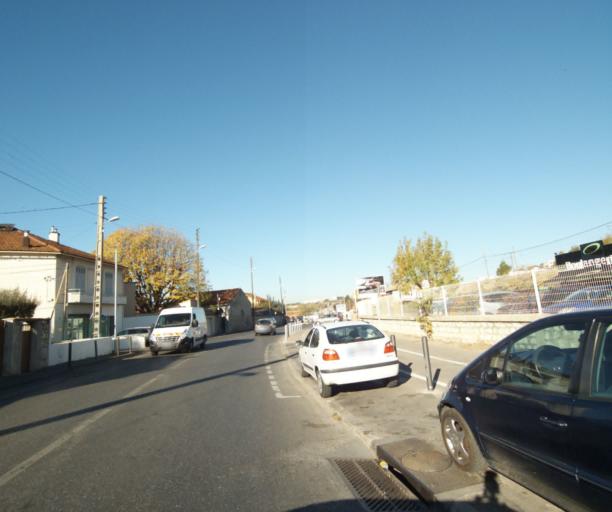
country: FR
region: Provence-Alpes-Cote d'Azur
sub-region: Departement des Bouches-du-Rhone
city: Marseille 11
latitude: 43.2891
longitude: 5.4278
